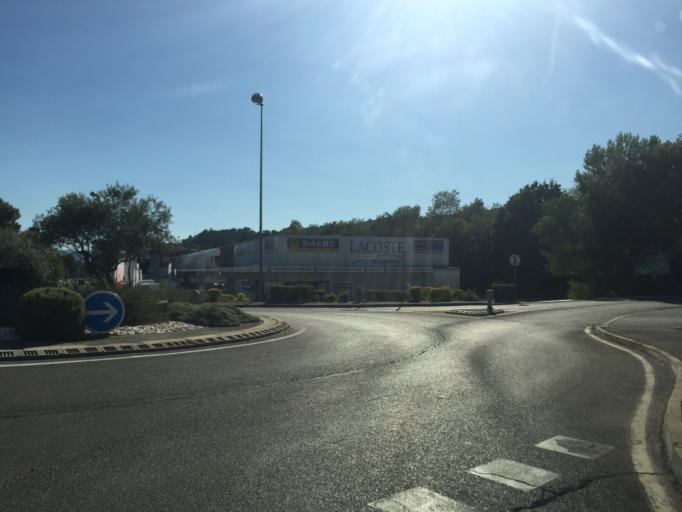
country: FR
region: Provence-Alpes-Cote d'Azur
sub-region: Departement des Alpes-de-Haute-Provence
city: Mallemoisson
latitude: 44.0703
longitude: 6.1778
